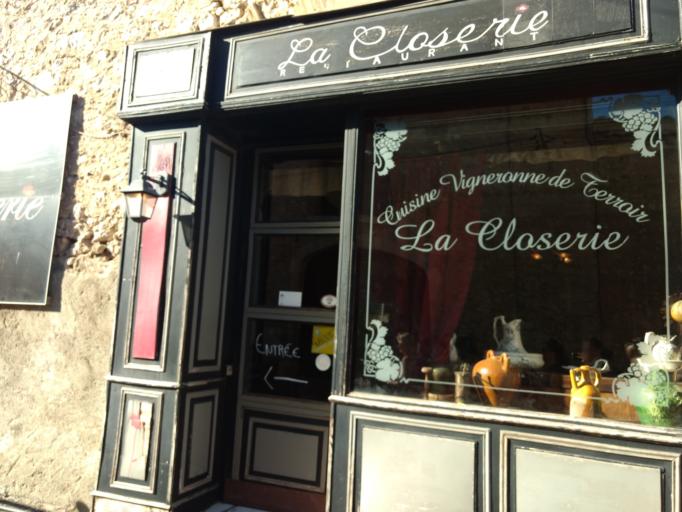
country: FR
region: Languedoc-Roussillon
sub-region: Departement de l'Aude
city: Leucate
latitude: 42.9096
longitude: 3.0302
